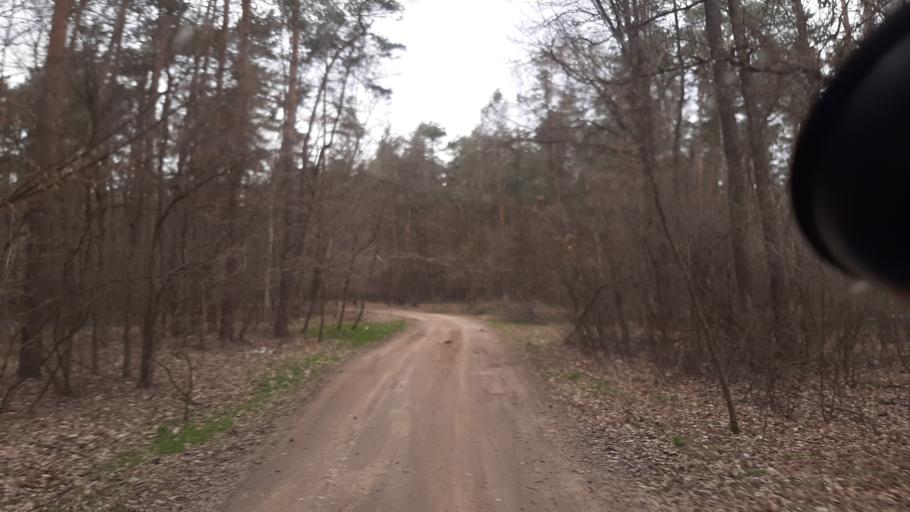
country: PL
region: Lublin Voivodeship
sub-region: Powiat lubartowski
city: Abramow
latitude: 51.4427
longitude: 22.3449
